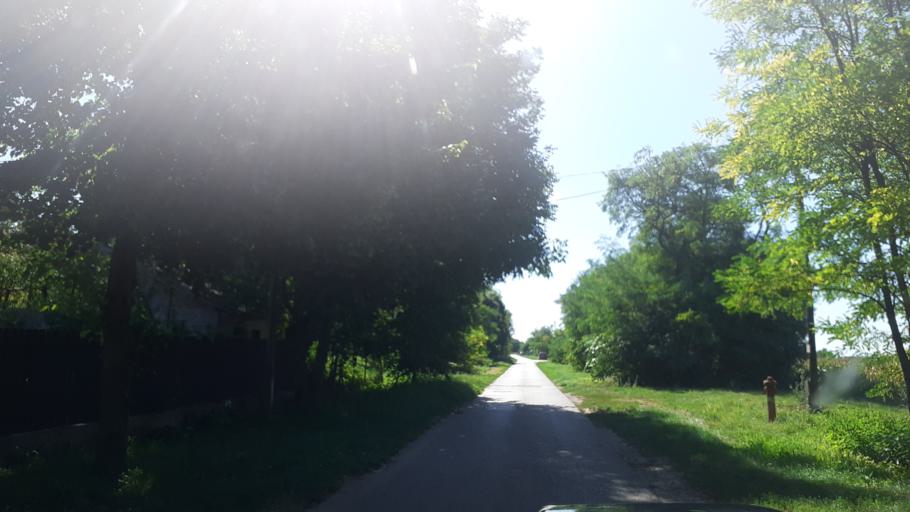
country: HU
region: Fejer
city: Baracska
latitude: 47.2799
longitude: 18.7732
